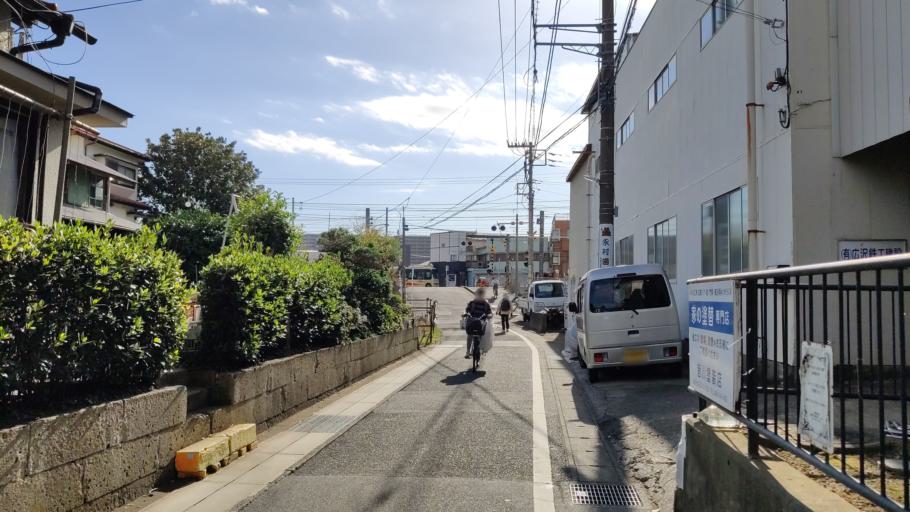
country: JP
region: Kanagawa
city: Fujisawa
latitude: 35.3376
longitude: 139.4964
